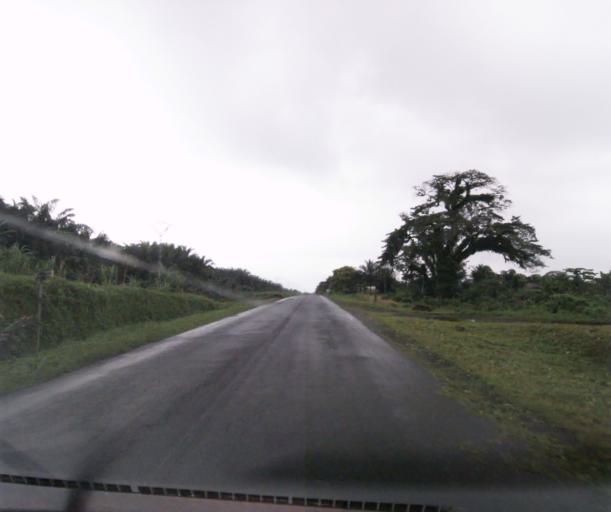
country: CM
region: South-West Province
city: Idenao
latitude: 4.1078
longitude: 8.9887
